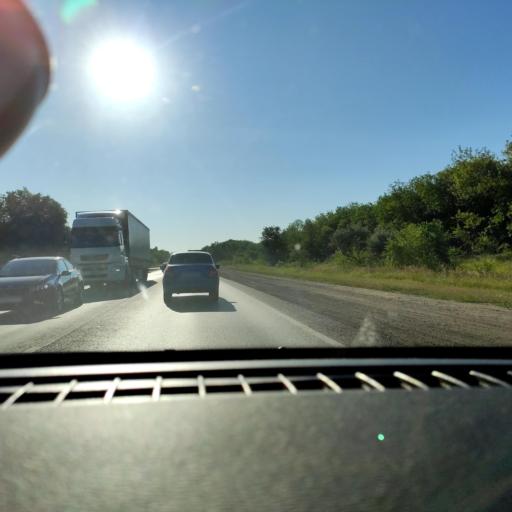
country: RU
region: Samara
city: Samara
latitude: 53.0811
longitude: 50.1001
